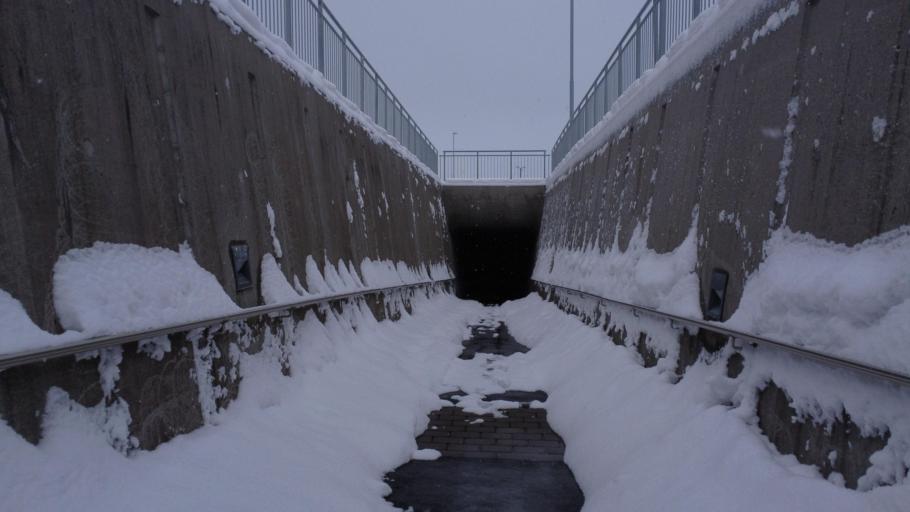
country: NO
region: Nordland
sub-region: Rana
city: Mo i Rana
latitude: 66.3101
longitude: 14.1326
